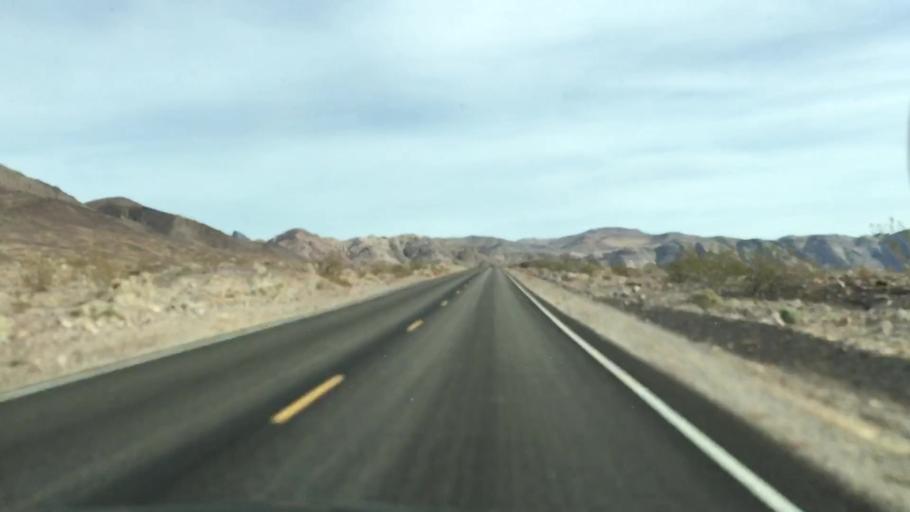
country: US
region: Nevada
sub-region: Nye County
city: Beatty
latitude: 36.7083
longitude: -116.9892
